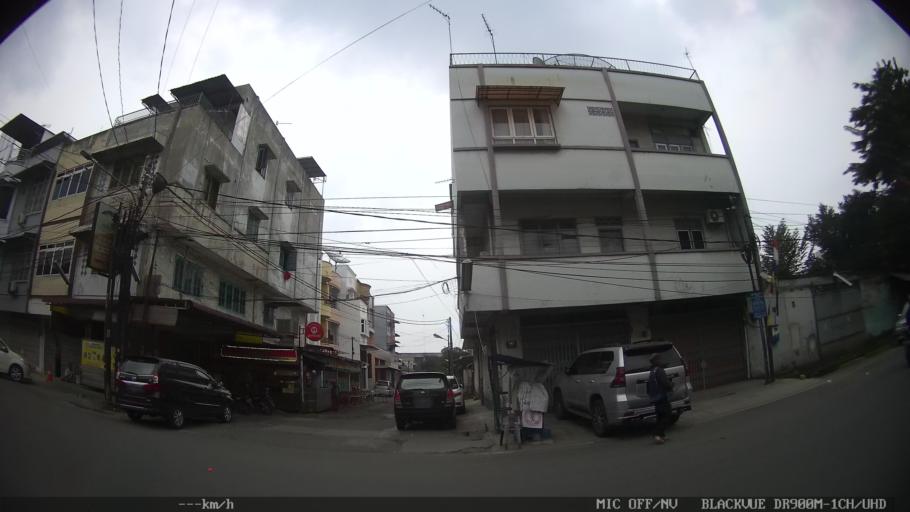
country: ID
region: North Sumatra
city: Medan
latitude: 3.5859
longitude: 98.6984
